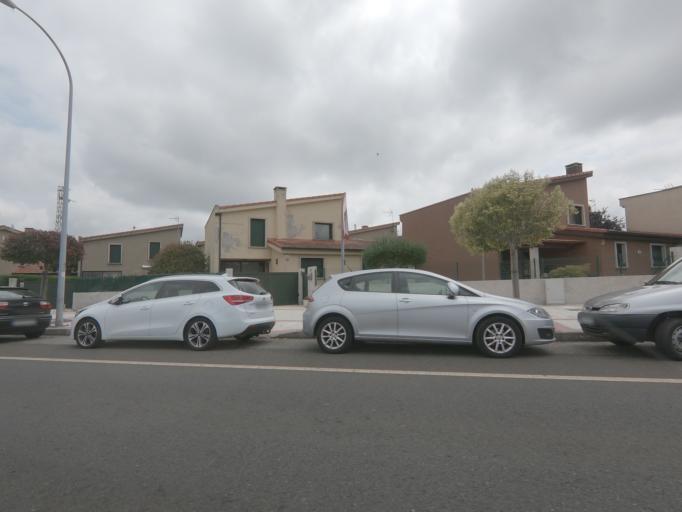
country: PT
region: Viana do Castelo
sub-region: Vila Nova de Cerveira
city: Vila Nova de Cerveira
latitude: 41.9453
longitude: -8.7778
